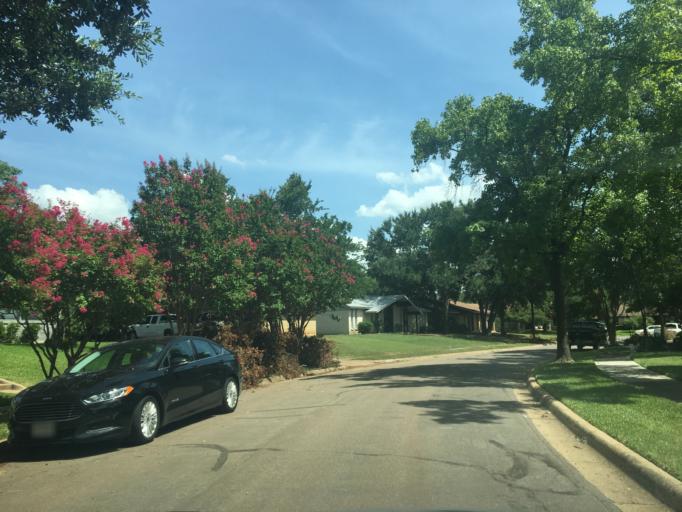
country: US
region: Texas
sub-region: Dallas County
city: Farmers Branch
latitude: 32.9168
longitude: -96.8520
